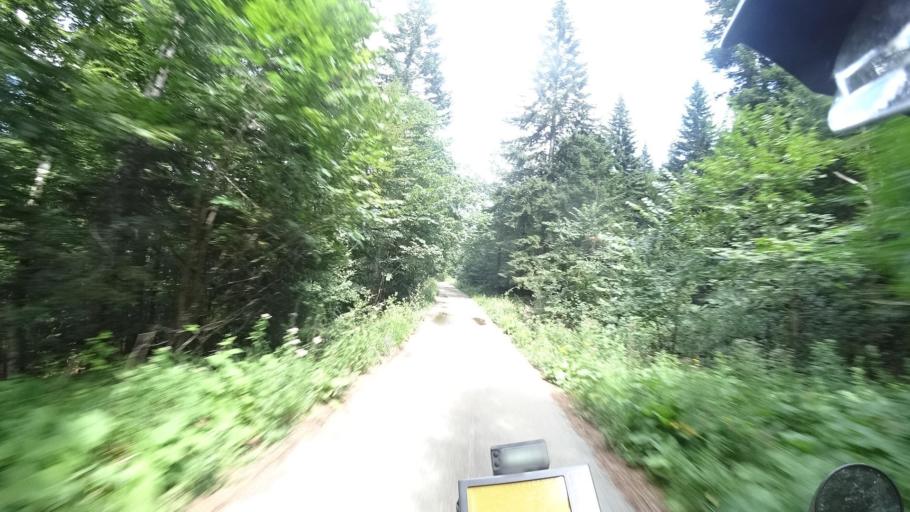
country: HR
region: Licko-Senjska
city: Senj
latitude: 45.1061
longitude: 15.0063
